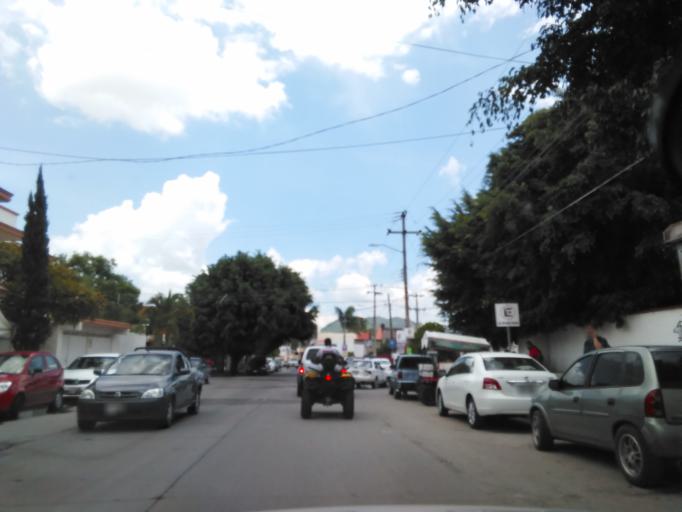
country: MX
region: Nayarit
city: Tepic
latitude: 21.4860
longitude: -104.8819
